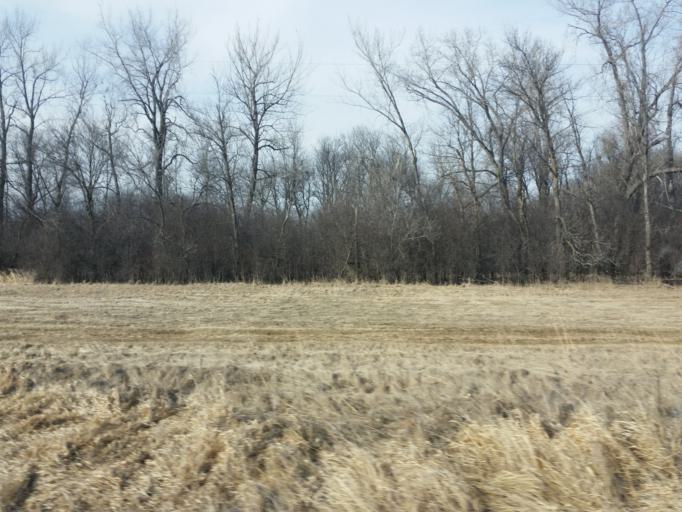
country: US
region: Minnesota
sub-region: Clay County
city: Barnesville
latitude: 46.4713
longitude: -96.3657
